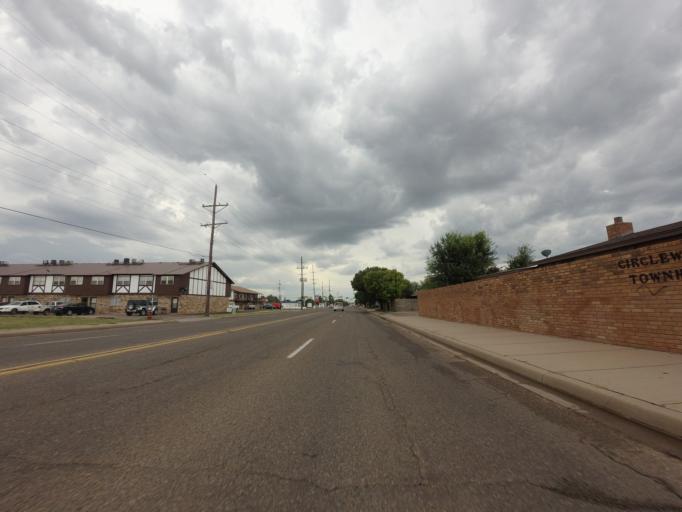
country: US
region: New Mexico
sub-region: Curry County
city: Clovis
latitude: 34.4138
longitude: -103.1790
